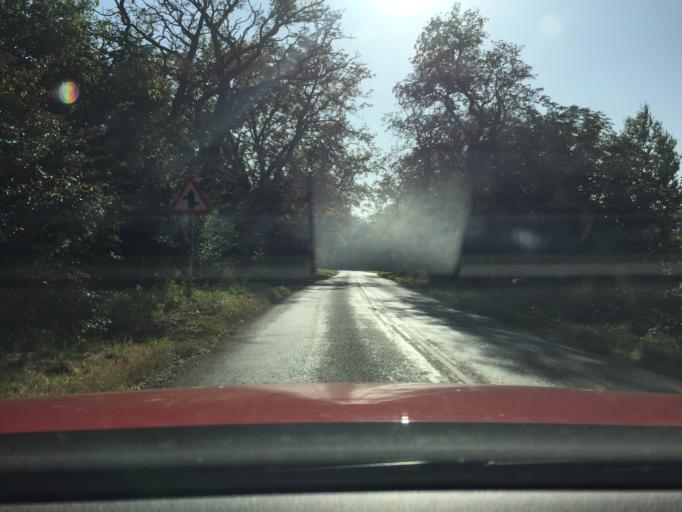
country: GB
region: England
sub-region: Leicestershire
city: Houghton on the Hill
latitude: 52.6541
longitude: -1.0122
